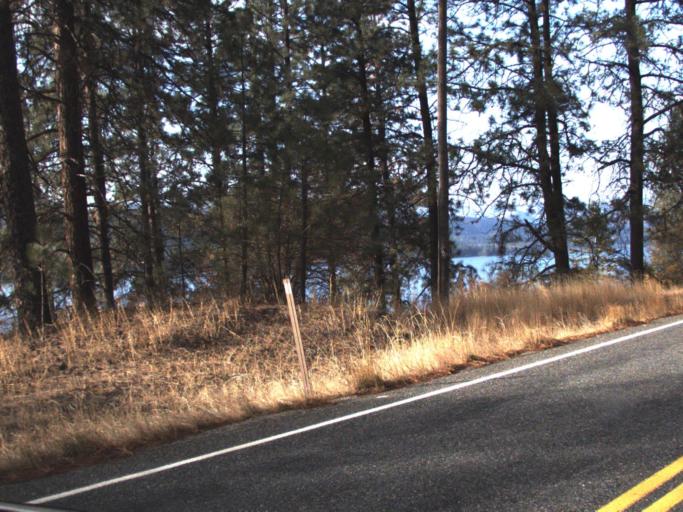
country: US
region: Washington
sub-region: Stevens County
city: Kettle Falls
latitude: 48.3648
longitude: -118.1637
